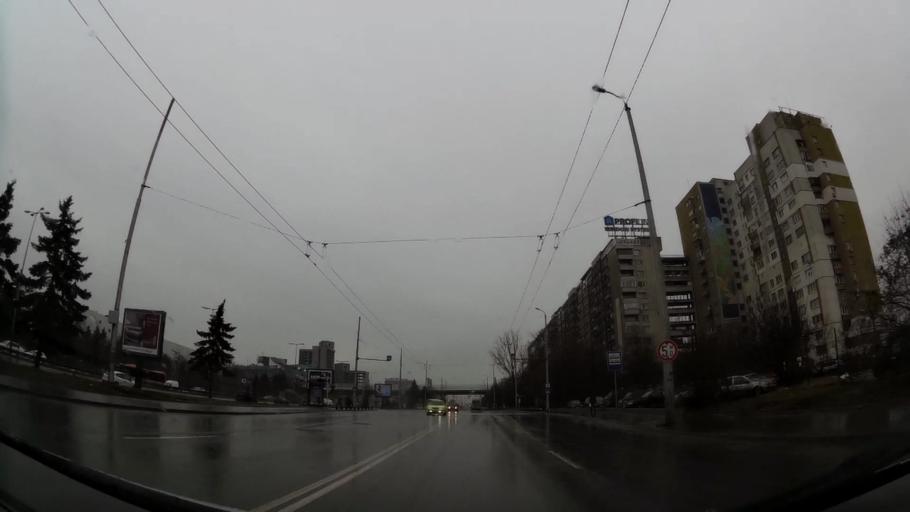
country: BG
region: Sofia-Capital
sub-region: Stolichna Obshtina
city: Sofia
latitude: 42.6660
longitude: 23.3713
